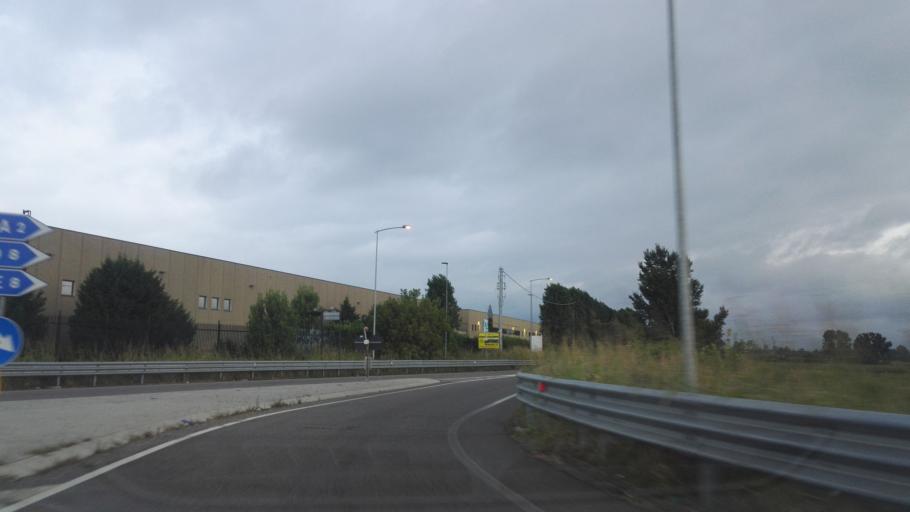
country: IT
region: Lombardy
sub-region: Citta metropolitana di Milano
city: Caleppio
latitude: 45.4432
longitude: 9.3877
